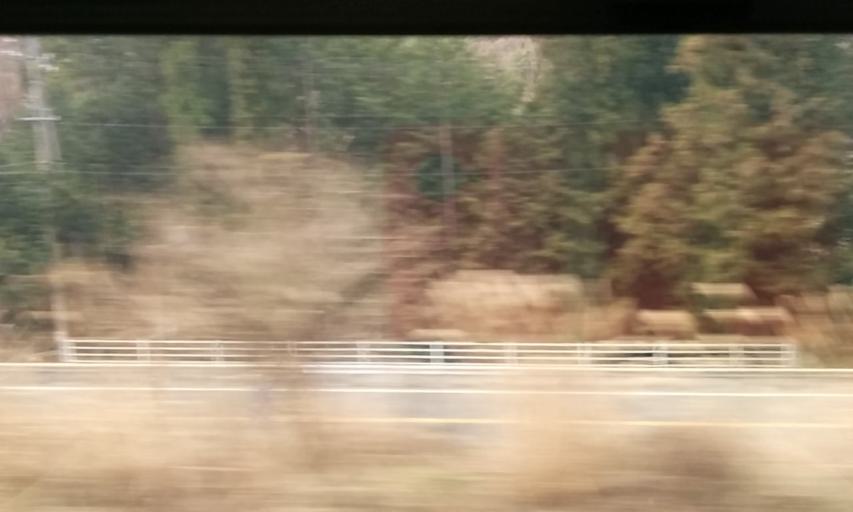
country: JP
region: Nagano
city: Shiojiri
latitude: 36.0403
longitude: 137.8876
